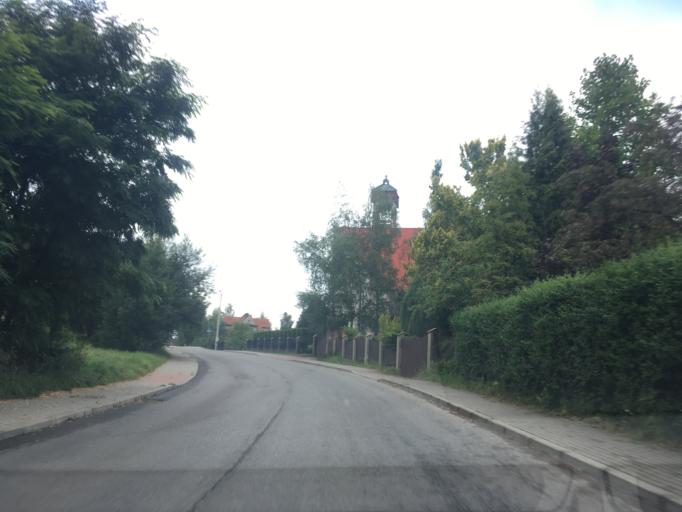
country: PL
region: Lesser Poland Voivodeship
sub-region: Powiat myslenicki
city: Dobczyce
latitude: 49.8470
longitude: 20.0800
